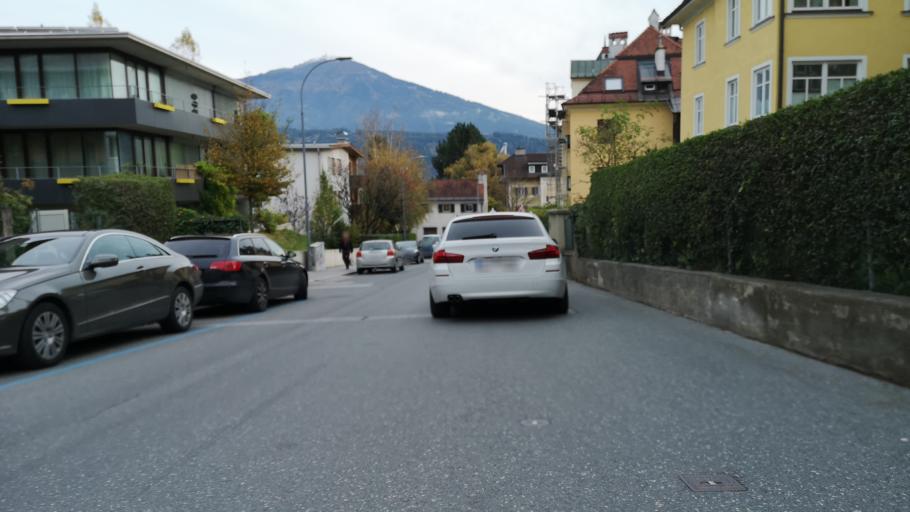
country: AT
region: Tyrol
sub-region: Innsbruck Stadt
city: Innsbruck
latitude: 47.2695
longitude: 11.3822
